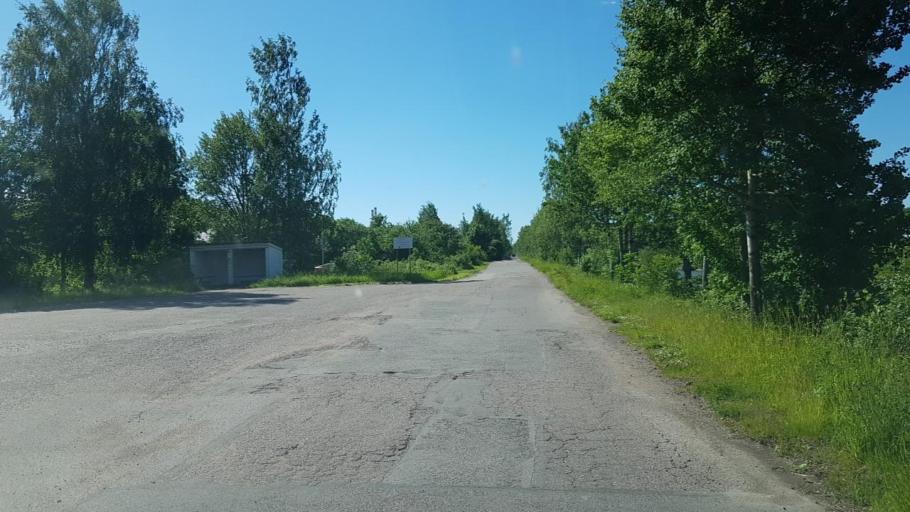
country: EE
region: Ida-Virumaa
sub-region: Narva linn
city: Narva
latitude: 59.3504
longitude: 28.1631
